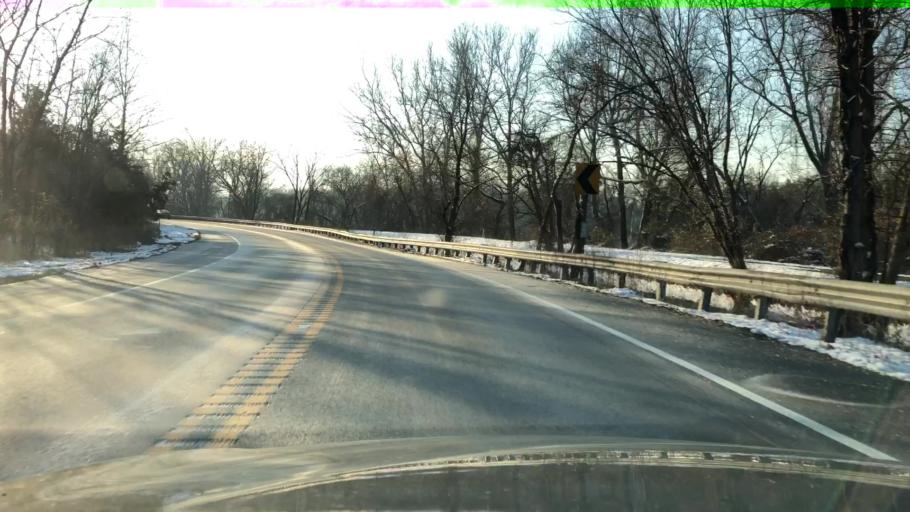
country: US
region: New Jersey
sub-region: Hunterdon County
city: Lambertville
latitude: 40.3308
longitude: -74.9252
